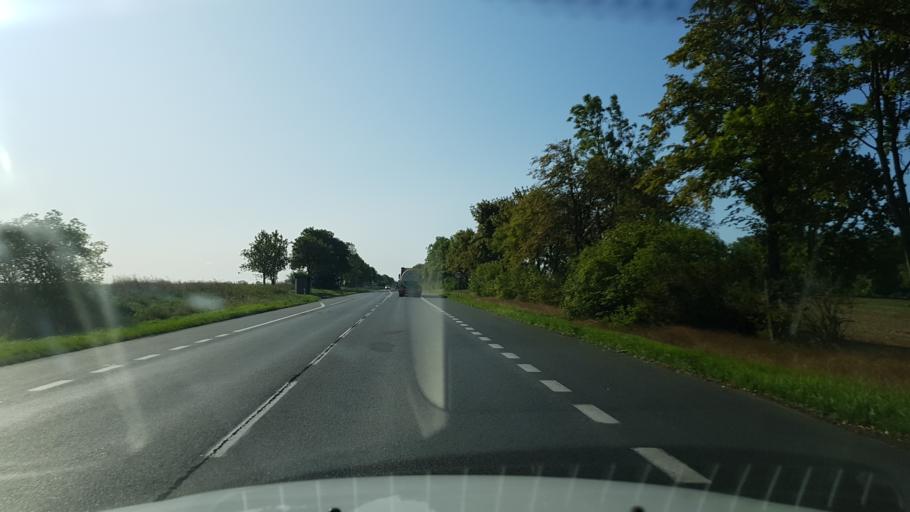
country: PL
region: West Pomeranian Voivodeship
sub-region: Powiat pyrzycki
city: Pyrzyce
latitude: 53.1122
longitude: 14.8949
